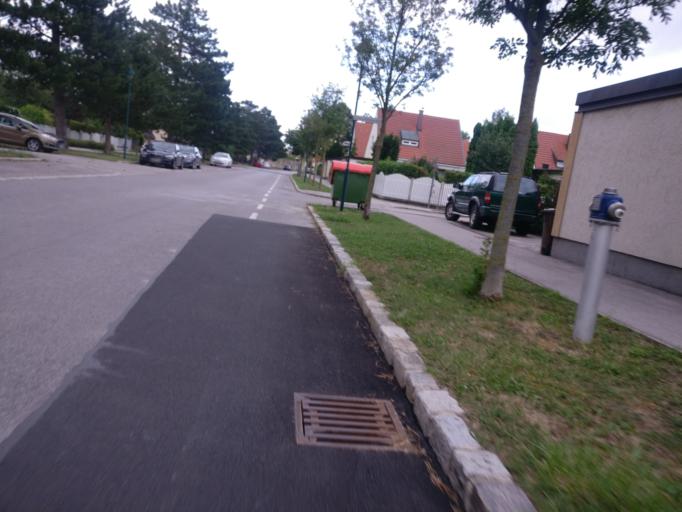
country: AT
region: Lower Austria
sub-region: Politischer Bezirk Modling
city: Laxenburg
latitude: 48.0701
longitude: 16.3517
